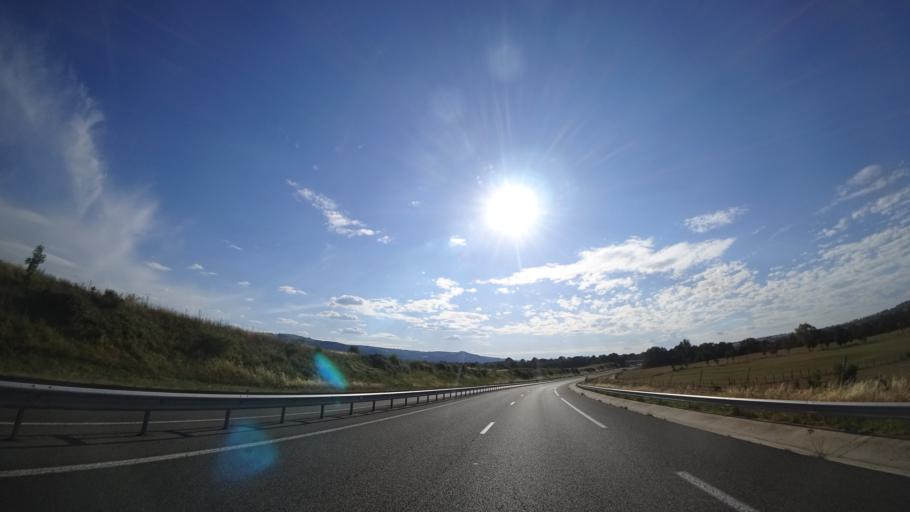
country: FR
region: Midi-Pyrenees
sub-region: Departement de l'Aveyron
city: Severac-le-Chateau
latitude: 44.3475
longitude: 2.9844
